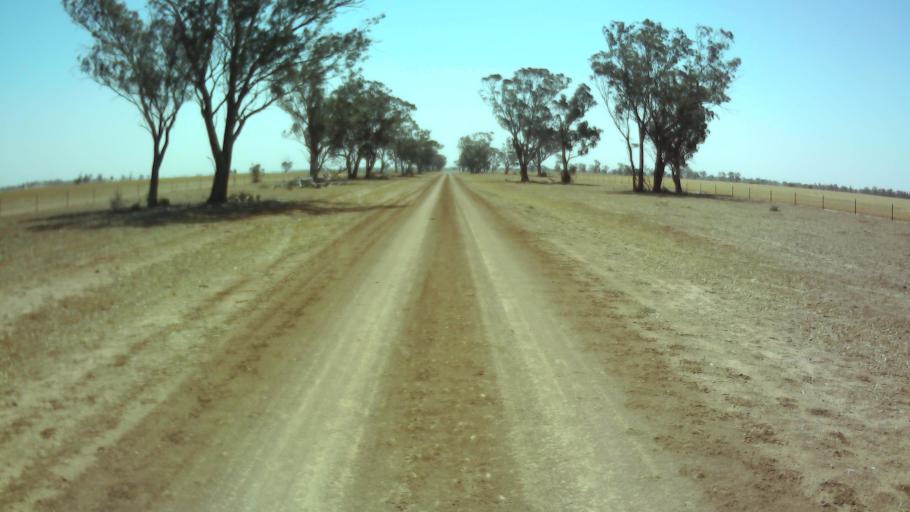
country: AU
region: New South Wales
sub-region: Weddin
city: Grenfell
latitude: -34.0072
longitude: 147.8859
